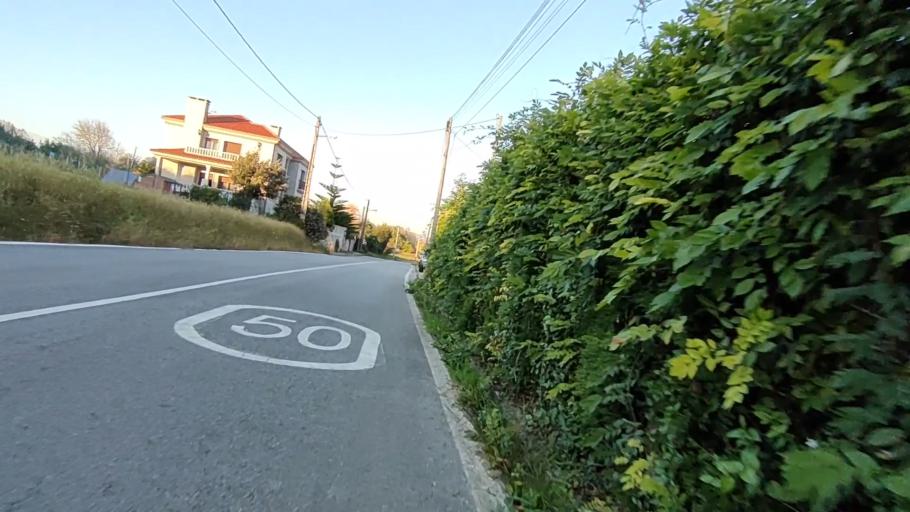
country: ES
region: Galicia
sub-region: Provincia da Coruna
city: Boiro
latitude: 42.6293
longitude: -8.8609
